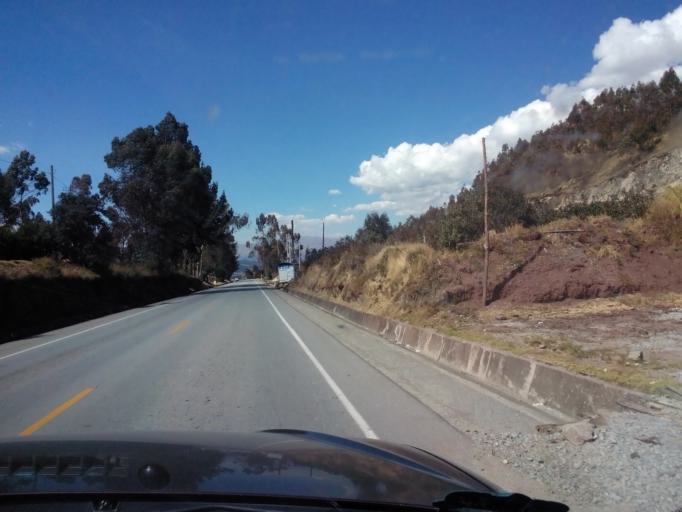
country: PE
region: Cusco
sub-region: Provincia de Anta
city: Ancahuasi
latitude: -13.4427
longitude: -72.3505
